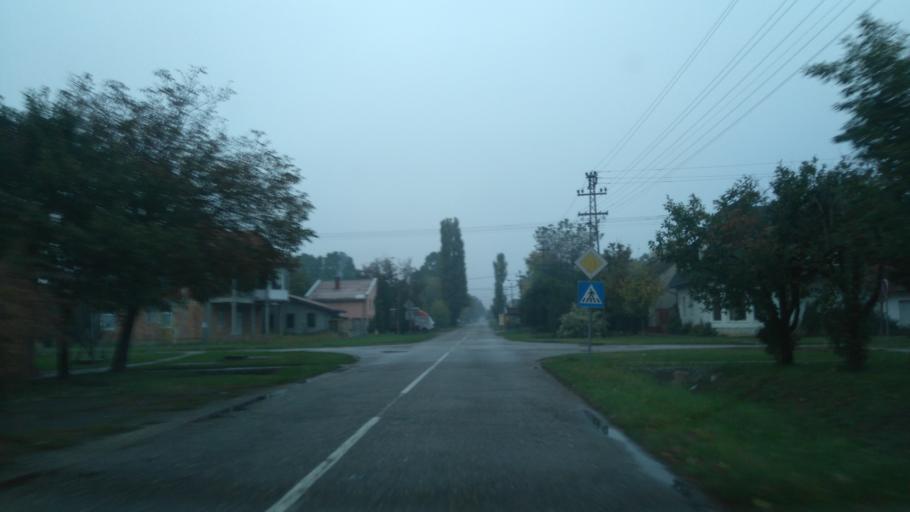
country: RS
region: Autonomna Pokrajina Vojvodina
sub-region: Juznobacki Okrug
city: Becej
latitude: 45.6164
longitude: 20.0396
